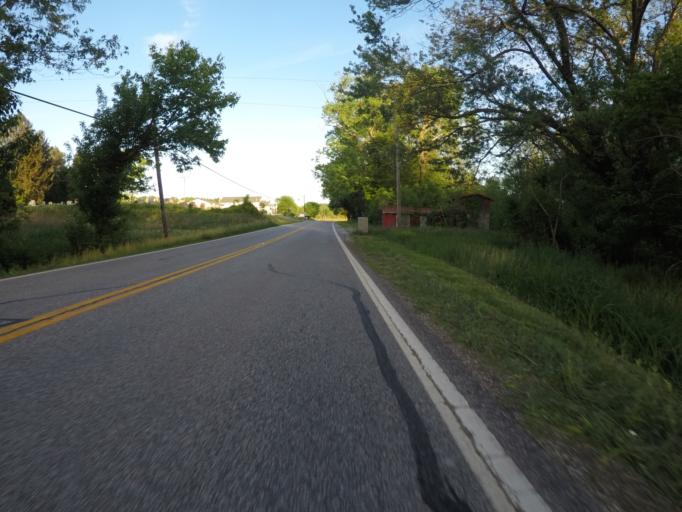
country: US
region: West Virginia
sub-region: Cabell County
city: Huntington
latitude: 38.4874
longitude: -82.4708
